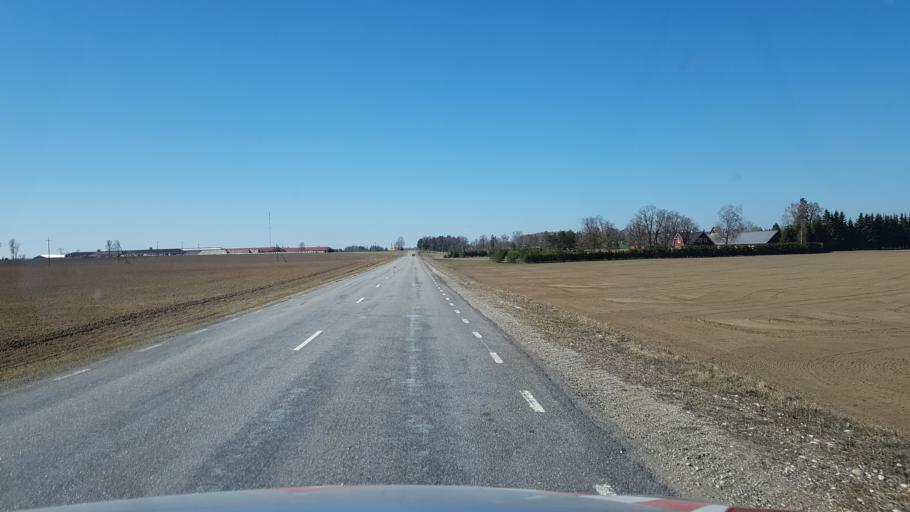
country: EE
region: Laeaene-Virumaa
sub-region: Vaeike-Maarja vald
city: Vaike-Maarja
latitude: 59.1610
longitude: 26.1912
